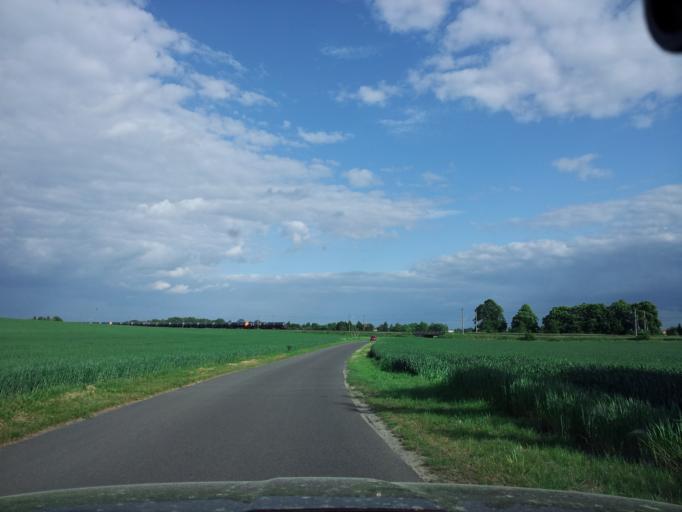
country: DE
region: Saxony-Anhalt
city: Seyda
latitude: 51.9580
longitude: 12.8973
